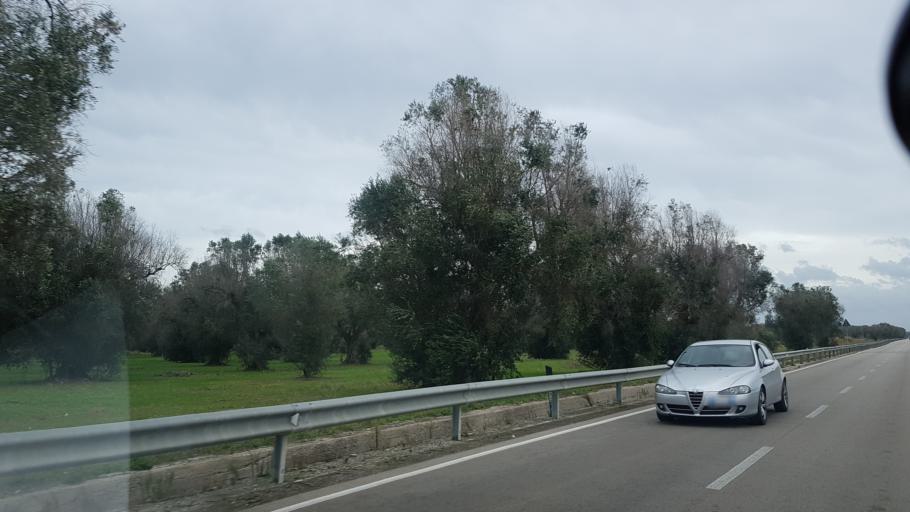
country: IT
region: Apulia
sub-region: Provincia di Brindisi
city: San Pancrazio Salentino
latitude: 40.4081
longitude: 17.8814
